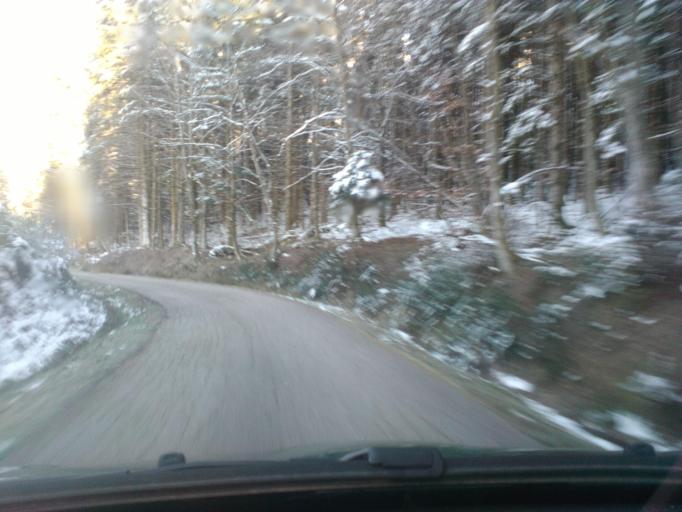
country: FR
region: Lorraine
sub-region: Departement des Vosges
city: Taintrux
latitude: 48.2191
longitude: 6.8745
